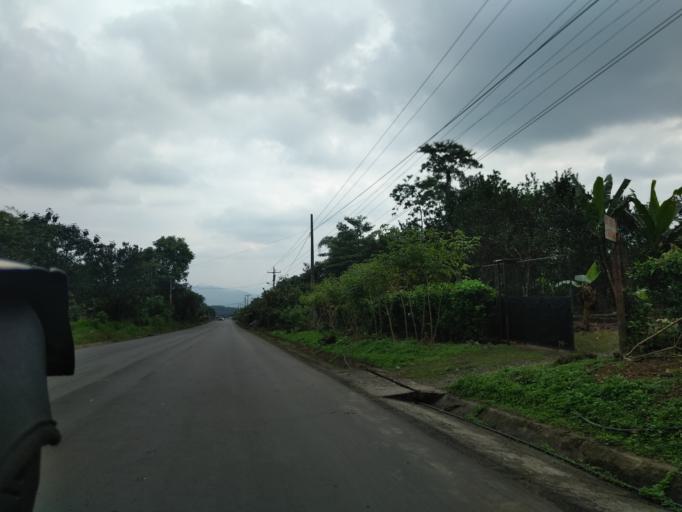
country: EC
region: Cotopaxi
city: La Mana
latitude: -0.8695
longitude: -79.1565
